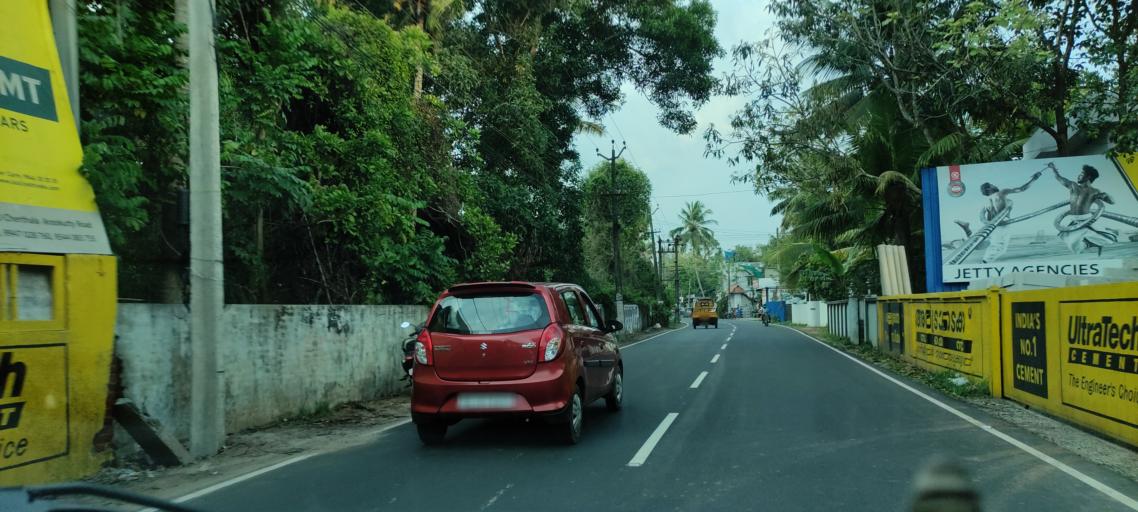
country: IN
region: Kerala
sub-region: Alappuzha
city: Kutiatodu
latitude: 9.8334
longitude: 76.3396
